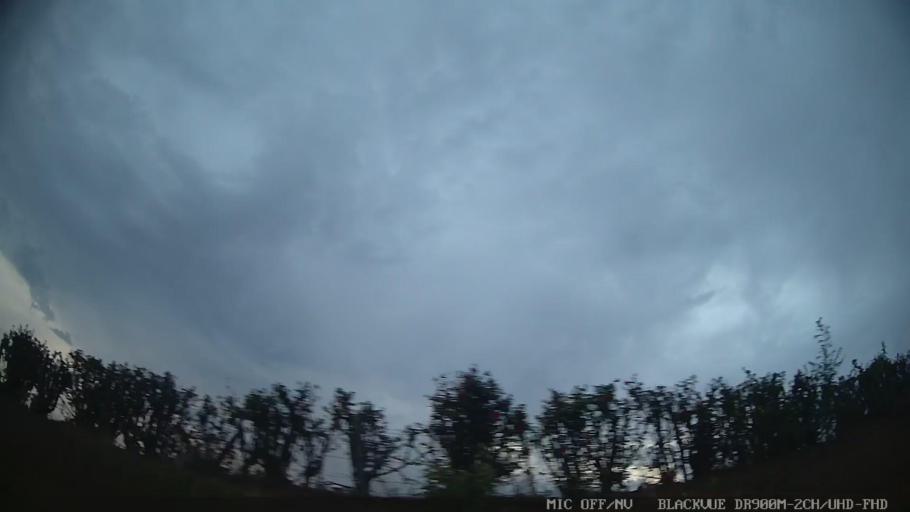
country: BR
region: Sao Paulo
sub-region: Louveira
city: Louveira
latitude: -23.1279
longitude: -46.9667
